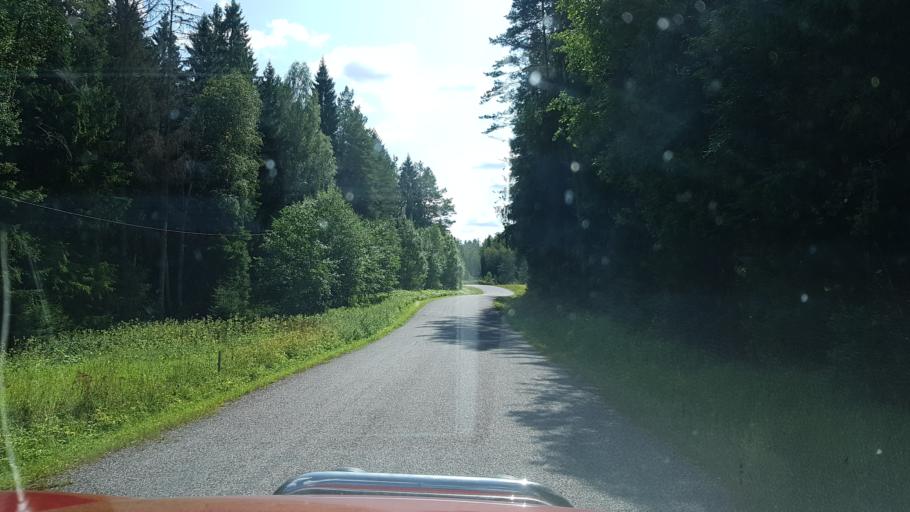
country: EE
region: Vorumaa
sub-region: Voru linn
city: Voru
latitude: 57.7288
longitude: 27.2097
